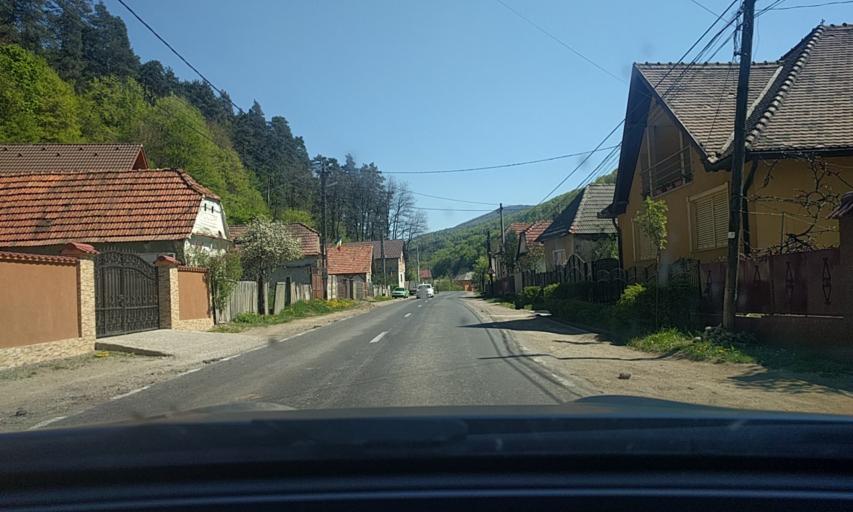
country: RO
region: Brasov
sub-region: Comuna Teliu
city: Teliu
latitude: 45.6961
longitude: 25.8666
